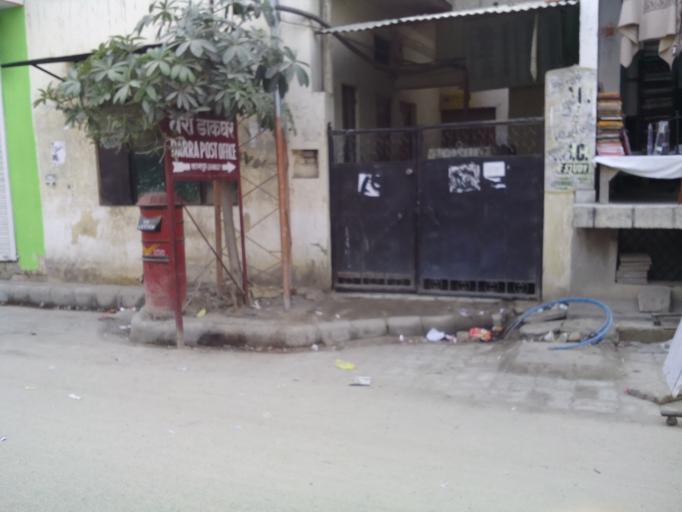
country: IN
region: Uttar Pradesh
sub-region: Kanpur
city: Kanpur
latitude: 26.4338
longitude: 80.3018
